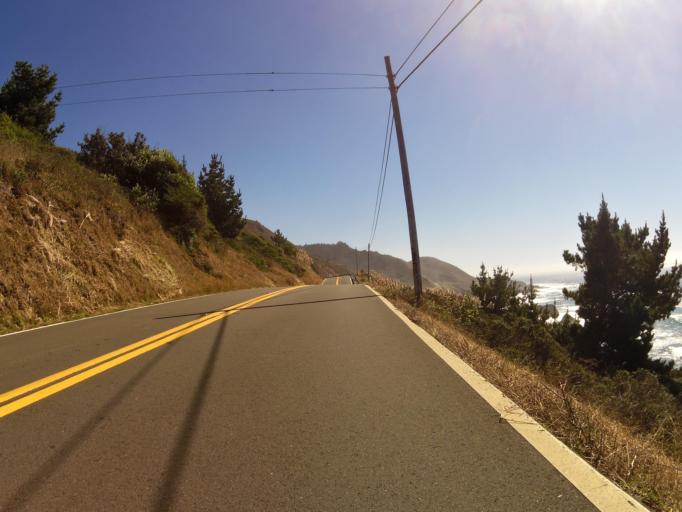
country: US
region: California
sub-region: Mendocino County
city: Fort Bragg
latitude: 39.6240
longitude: -123.7821
